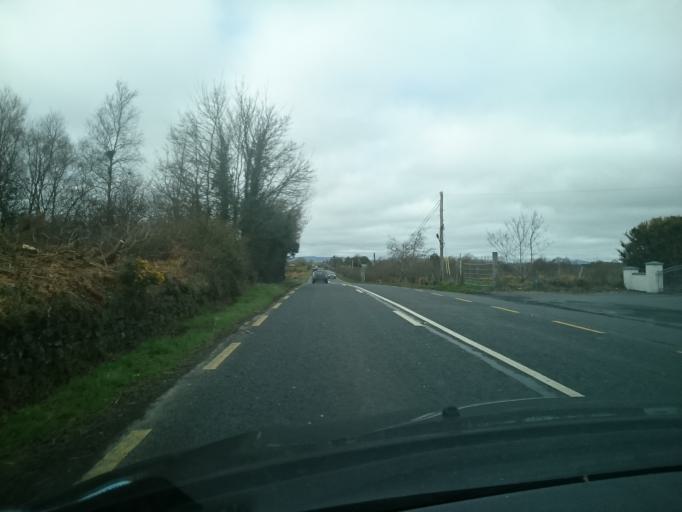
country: IE
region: Connaught
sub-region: Maigh Eo
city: Castlebar
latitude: 53.8166
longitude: -9.1619
